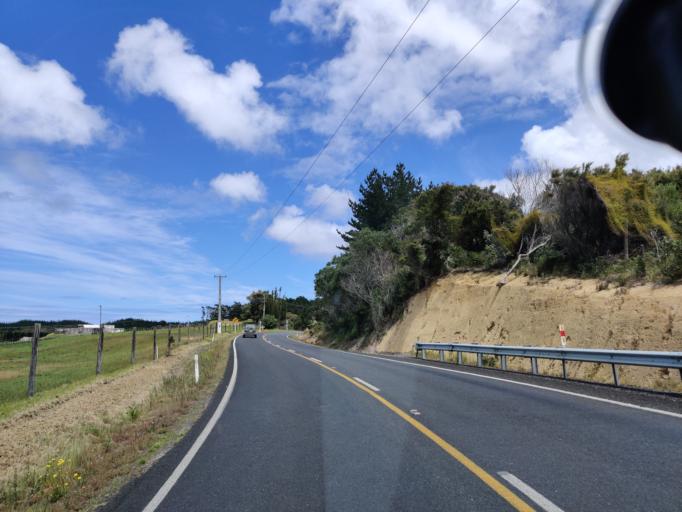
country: NZ
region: Northland
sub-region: Far North District
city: Kaitaia
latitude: -34.8875
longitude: 173.1621
